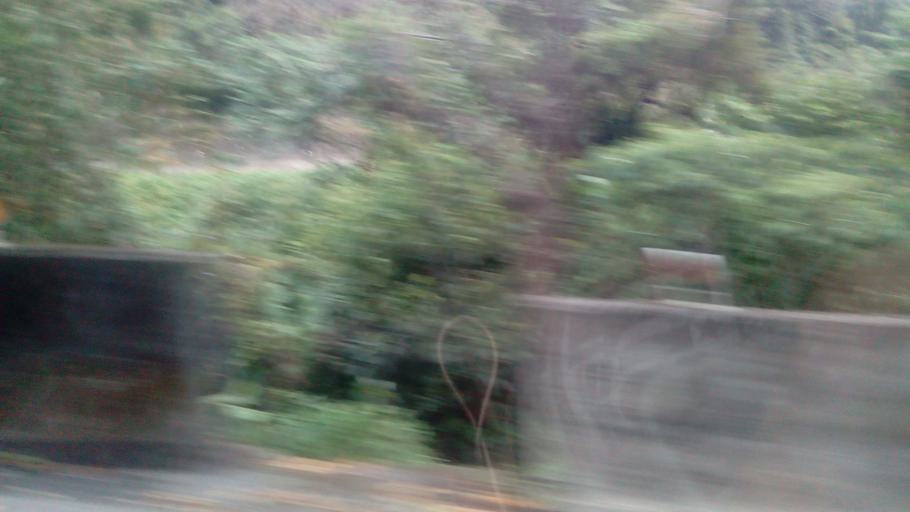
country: TW
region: Taiwan
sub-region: Yilan
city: Yilan
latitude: 24.5806
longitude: 121.4946
